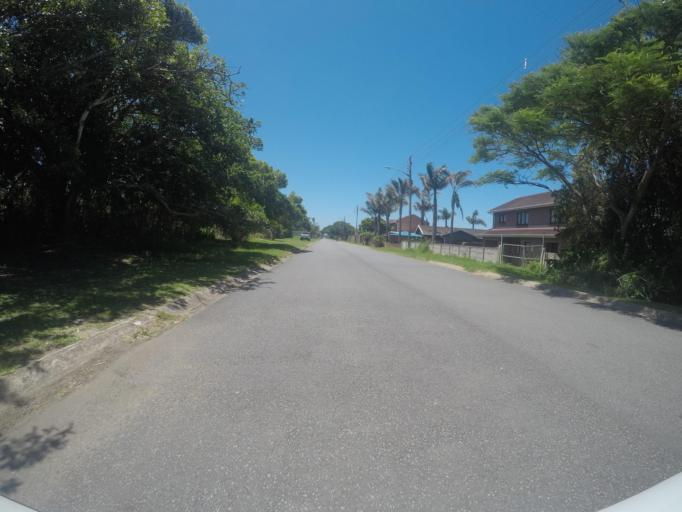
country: ZA
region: Eastern Cape
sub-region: Buffalo City Metropolitan Municipality
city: East London
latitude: -32.9508
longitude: 28.0104
